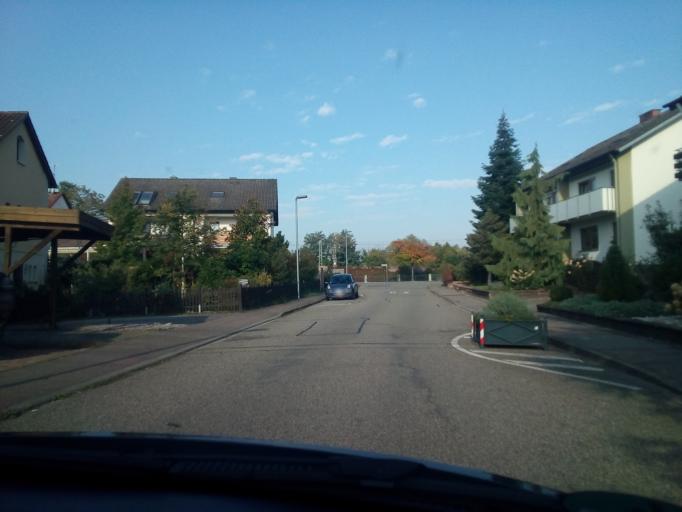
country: DE
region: Baden-Wuerttemberg
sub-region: Karlsruhe Region
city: Buhl
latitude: 48.6936
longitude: 8.1284
